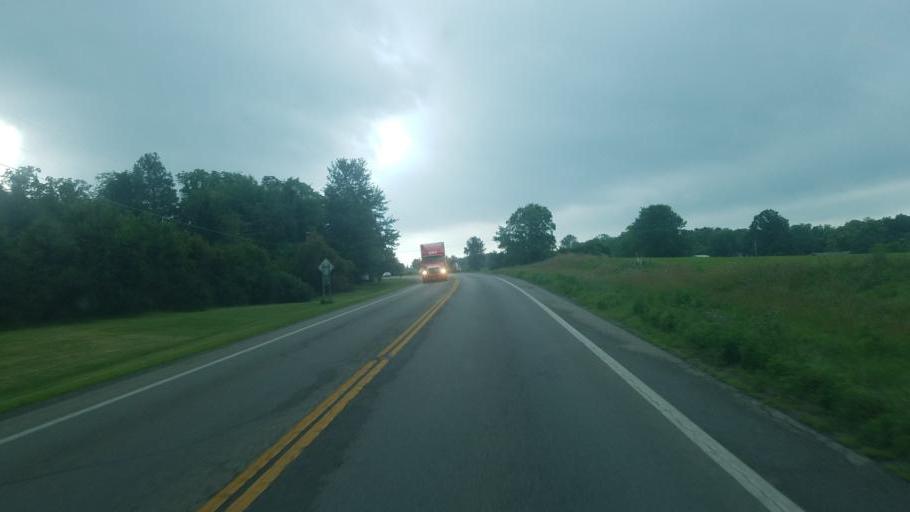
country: US
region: Ohio
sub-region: Logan County
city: Russells Point
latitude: 40.5554
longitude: -83.8353
